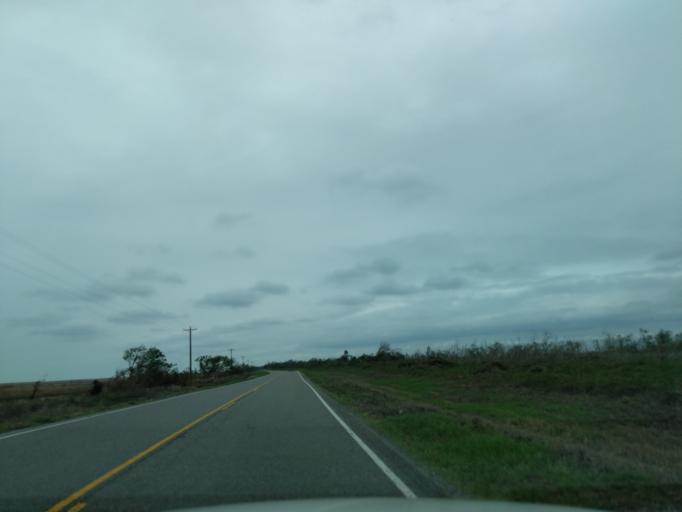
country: US
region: Louisiana
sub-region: Cameron Parish
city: Cameron
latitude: 29.7865
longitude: -93.1653
